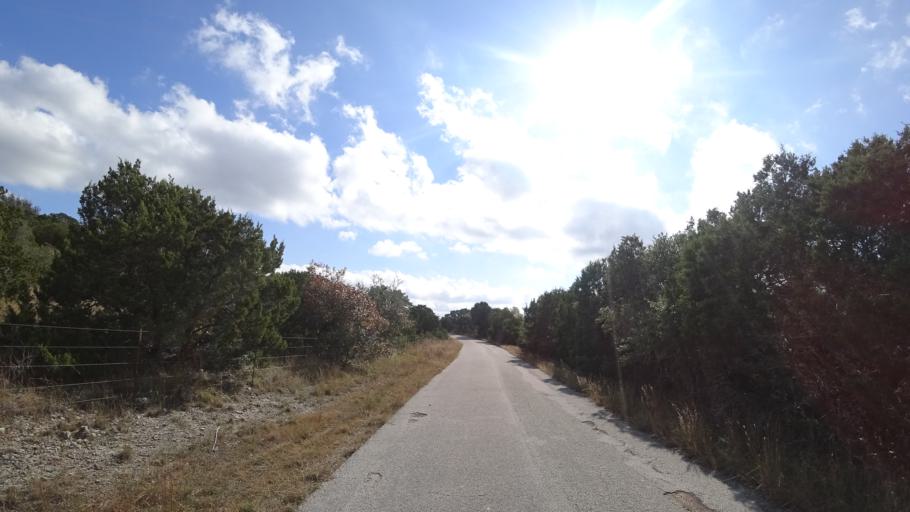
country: US
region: Texas
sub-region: Travis County
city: Bee Cave
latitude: 30.2576
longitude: -97.9413
